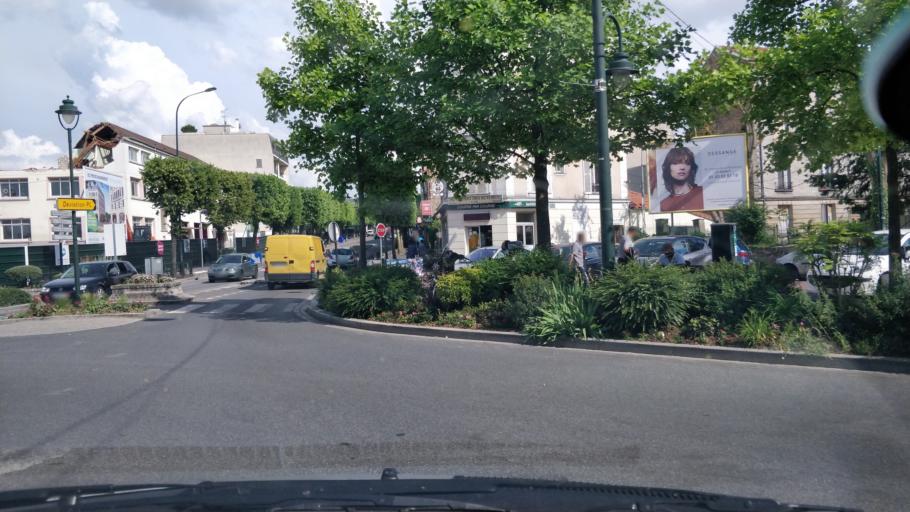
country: FR
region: Ile-de-France
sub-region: Departement de Seine-Saint-Denis
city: Le Raincy
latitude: 48.8993
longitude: 2.5175
